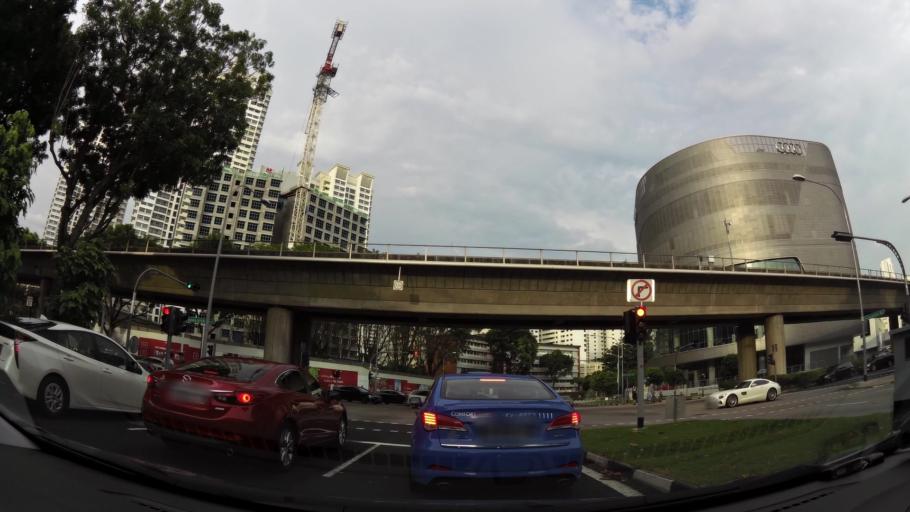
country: SG
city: Singapore
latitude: 1.2918
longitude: 103.8082
